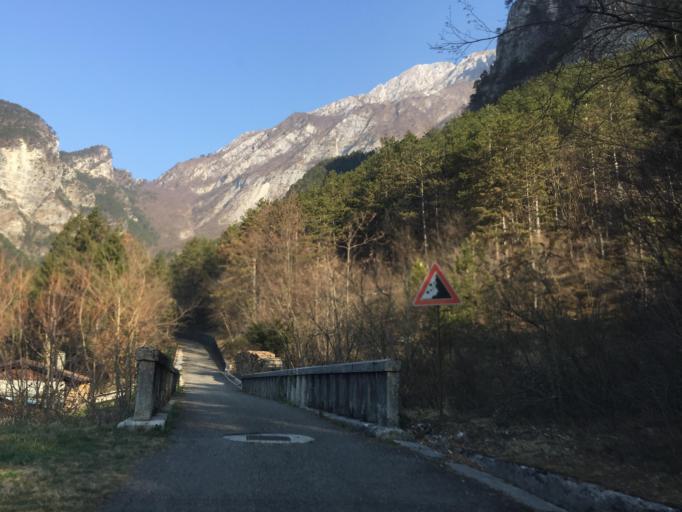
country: IT
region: Friuli Venezia Giulia
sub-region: Provincia di Udine
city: Amaro
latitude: 46.3783
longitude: 13.0919
